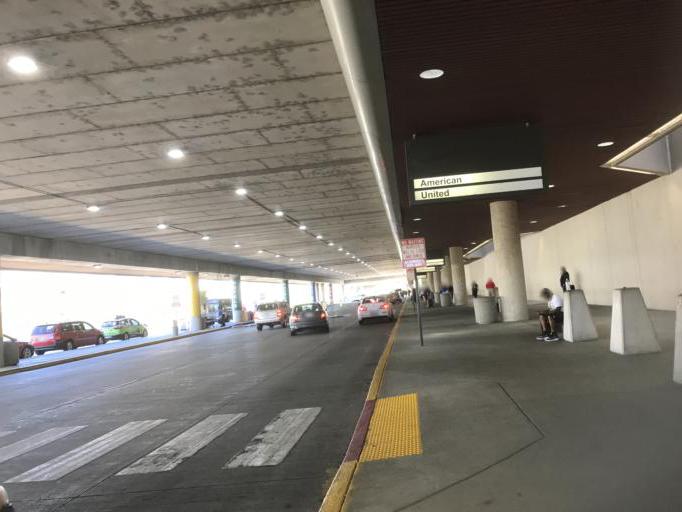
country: US
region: Kentucky
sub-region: Jefferson County
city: Audubon Park
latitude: 38.1860
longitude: -85.7425
